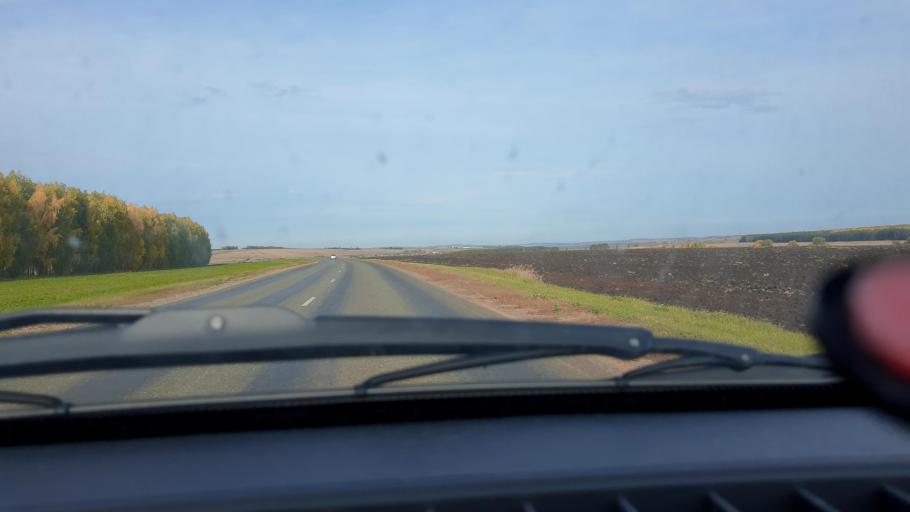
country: RU
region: Bashkortostan
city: Chekmagush
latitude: 54.9764
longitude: 54.5737
